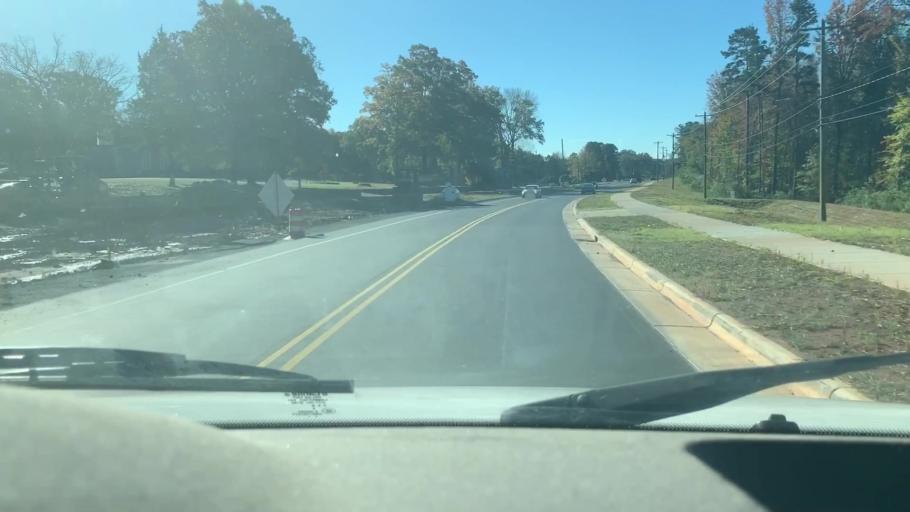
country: US
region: North Carolina
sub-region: Mecklenburg County
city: Charlotte
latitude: 35.3004
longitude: -80.8557
